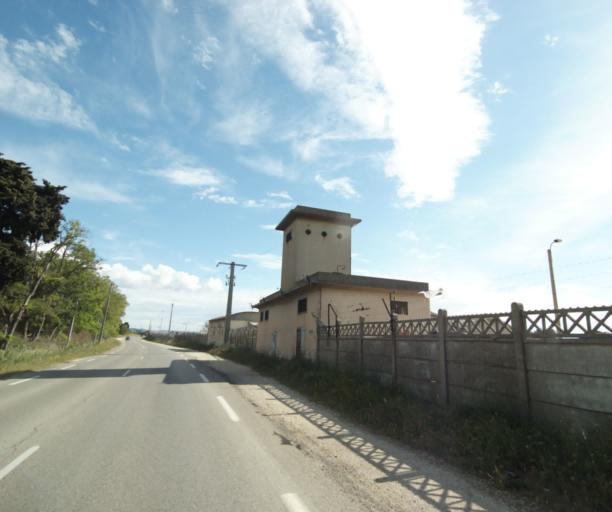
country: FR
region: Provence-Alpes-Cote d'Azur
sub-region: Departement des Bouches-du-Rhone
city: Rognac
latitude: 43.4814
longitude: 5.2303
